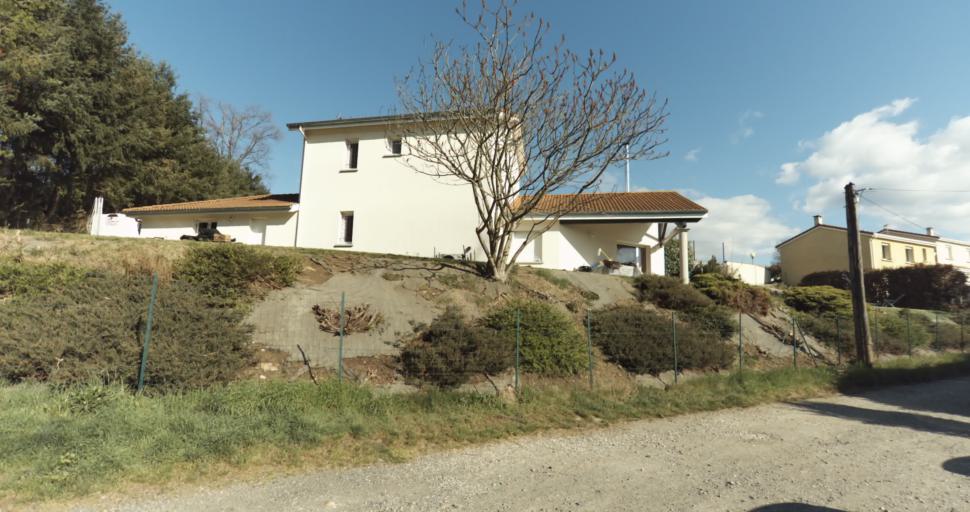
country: FR
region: Rhone-Alpes
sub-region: Departement de la Loire
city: Sorbiers
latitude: 45.4753
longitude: 4.4536
